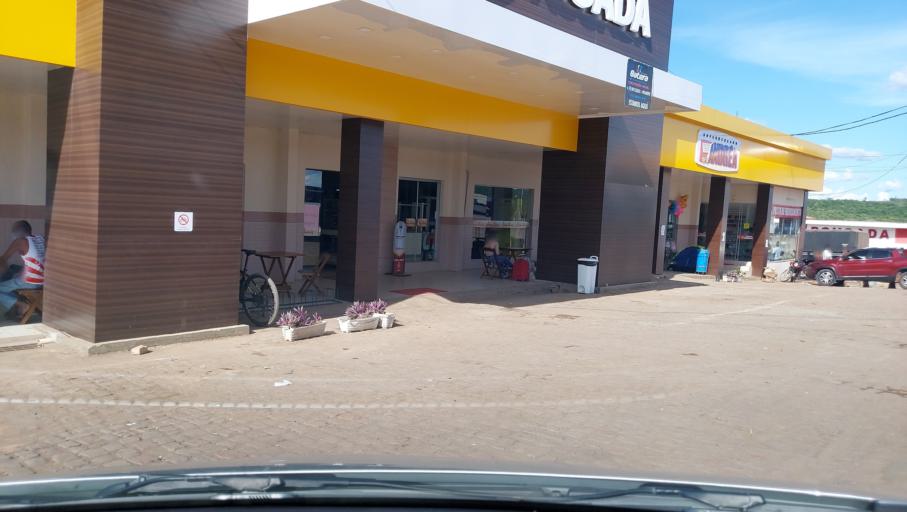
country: BR
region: Bahia
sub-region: Seabra
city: Seabra
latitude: -12.4573
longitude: -41.6457
